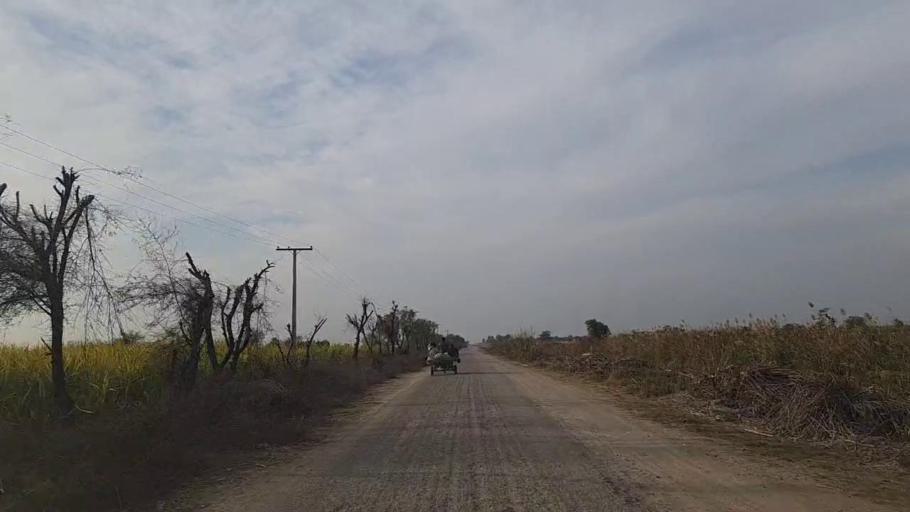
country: PK
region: Sindh
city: Daur
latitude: 26.4894
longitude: 68.4606
